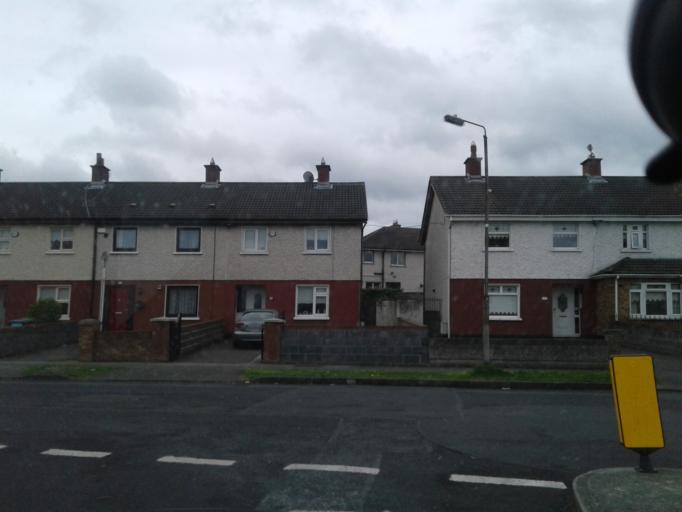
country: IE
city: Jobstown
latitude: 53.2778
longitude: -6.4015
